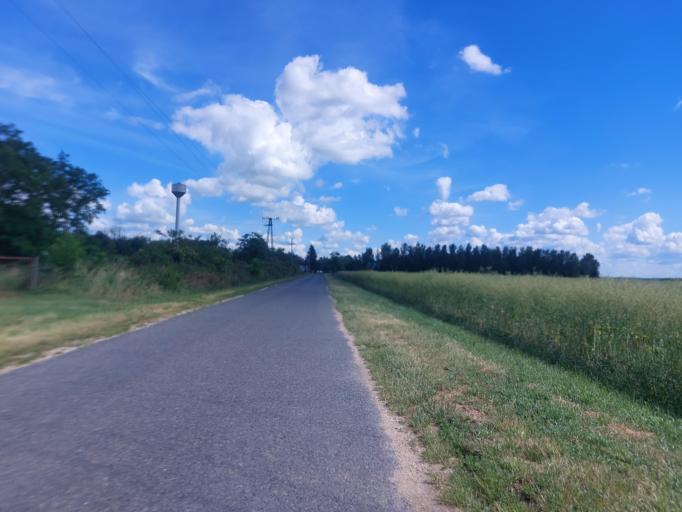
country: HU
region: Veszprem
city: Devecser
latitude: 47.2008
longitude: 17.3484
